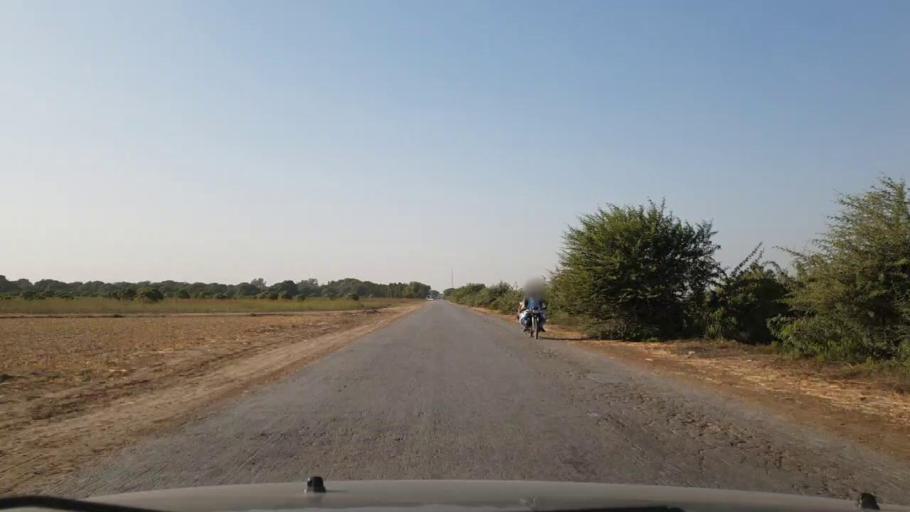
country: PK
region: Sindh
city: Chambar
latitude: 25.2050
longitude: 68.7890
